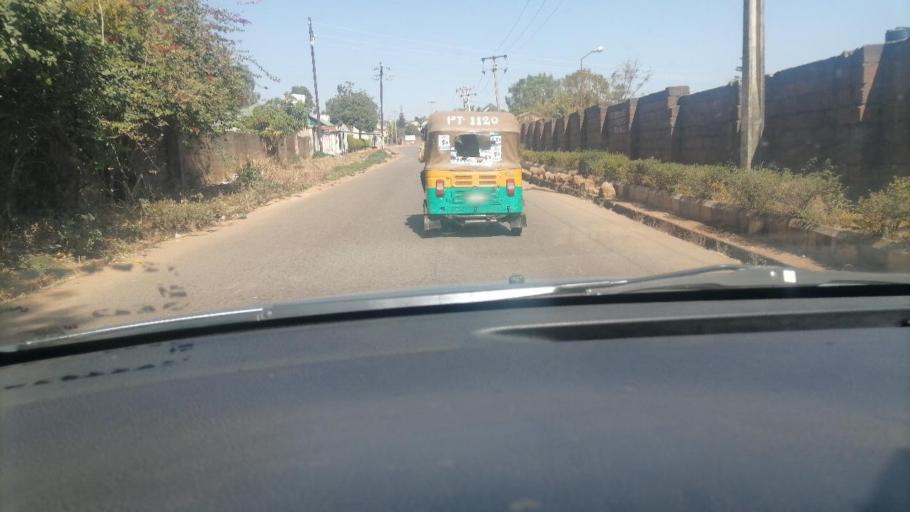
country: NG
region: Plateau
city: Jos
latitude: 9.8658
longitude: 8.9067
